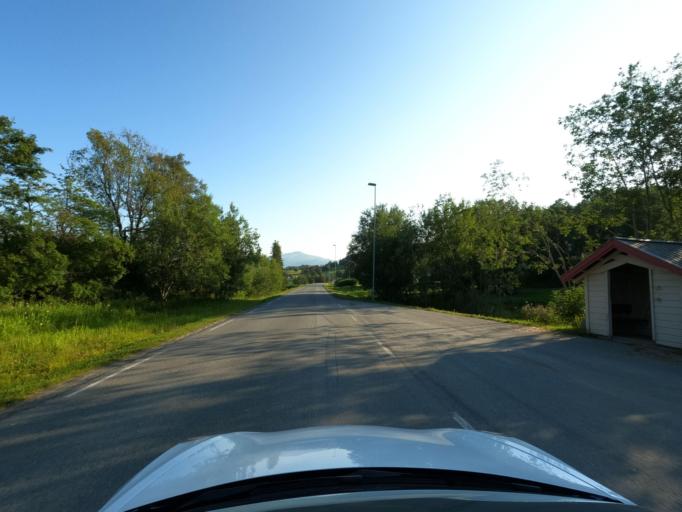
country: NO
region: Nordland
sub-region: Evenes
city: Randa
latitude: 68.4824
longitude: 16.8917
